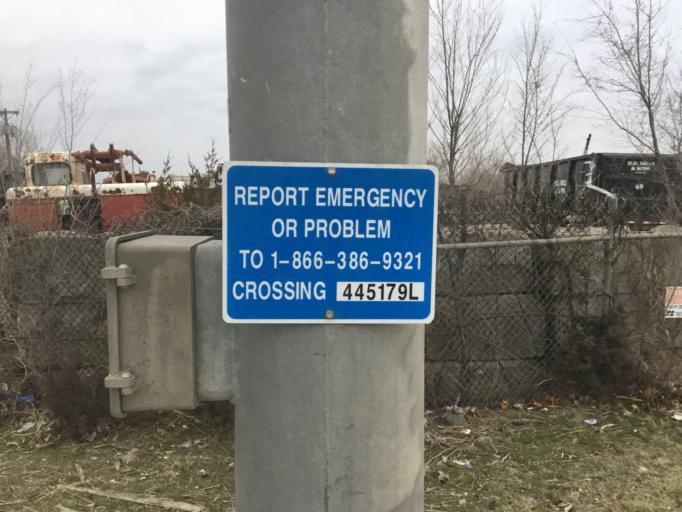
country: US
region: Kansas
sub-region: Sedgwick County
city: Wichita
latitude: 37.6458
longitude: -97.3891
